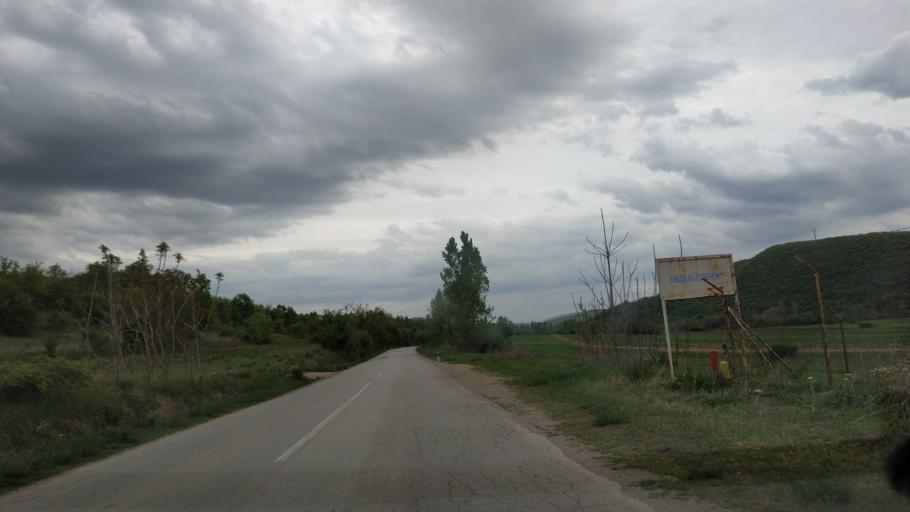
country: RS
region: Central Serbia
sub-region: Nisavski Okrug
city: Aleksinac
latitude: 43.5946
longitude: 21.6912
